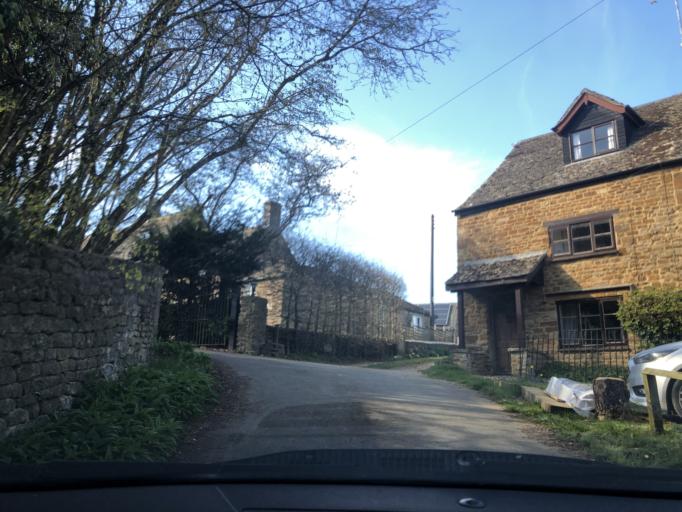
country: GB
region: England
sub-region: Oxfordshire
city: Hook Norton
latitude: 51.9967
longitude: -1.4917
